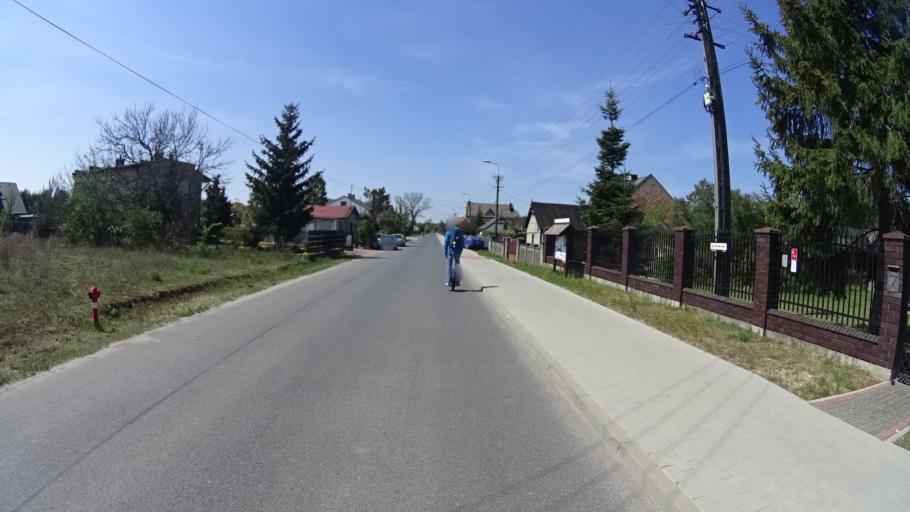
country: PL
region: Masovian Voivodeship
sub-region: Powiat warszawski zachodni
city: Truskaw
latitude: 52.2825
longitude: 20.7416
